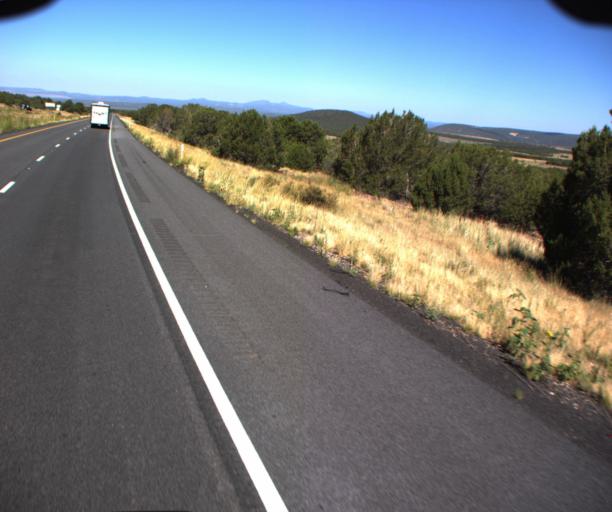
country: US
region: Arizona
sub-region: Coconino County
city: Williams
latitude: 35.2154
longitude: -112.3616
